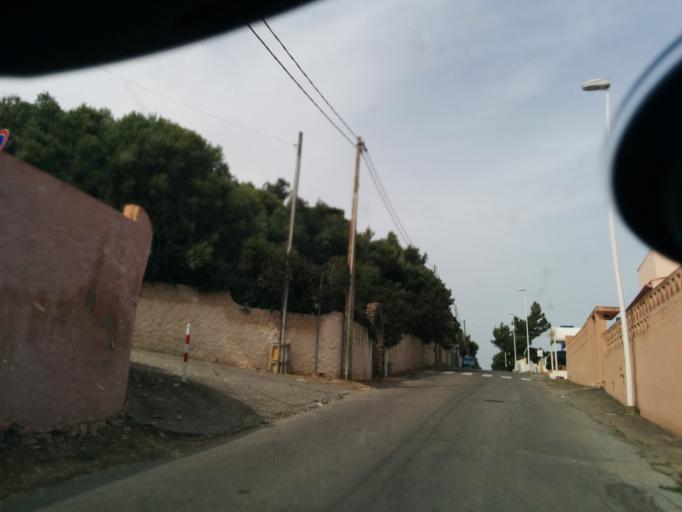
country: IT
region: Sardinia
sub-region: Provincia di Carbonia-Iglesias
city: Sant'Antioco
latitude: 38.9999
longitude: 8.4472
